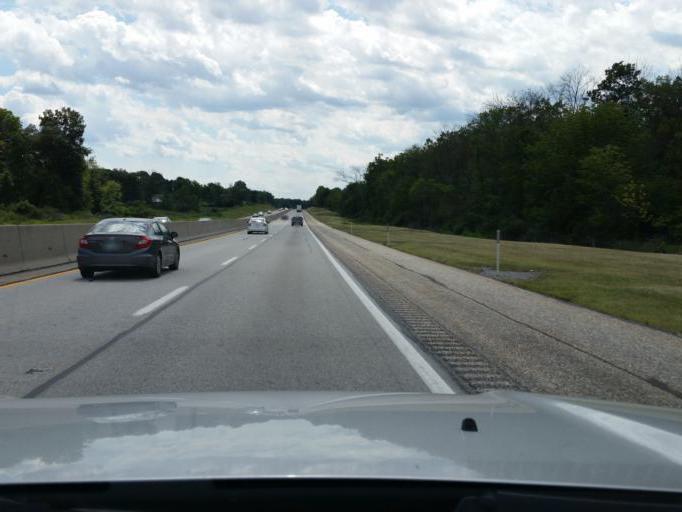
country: US
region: Pennsylvania
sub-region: Franklin County
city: Doylestown
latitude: 40.1357
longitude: -77.7357
